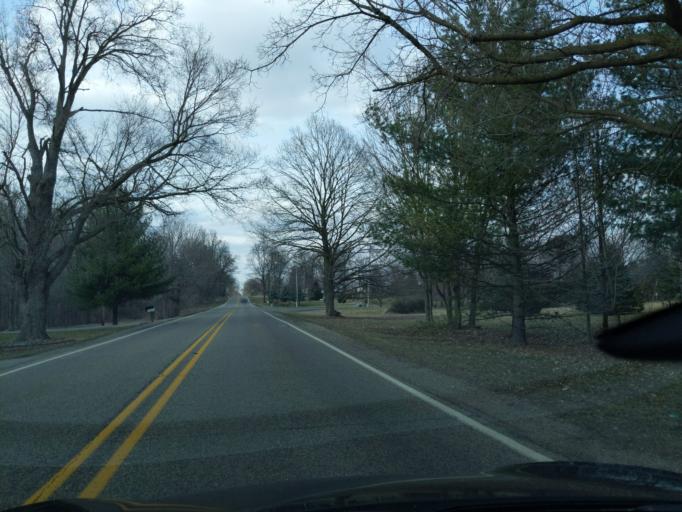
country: US
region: Michigan
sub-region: Jackson County
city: Jackson
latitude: 42.3118
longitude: -84.4136
